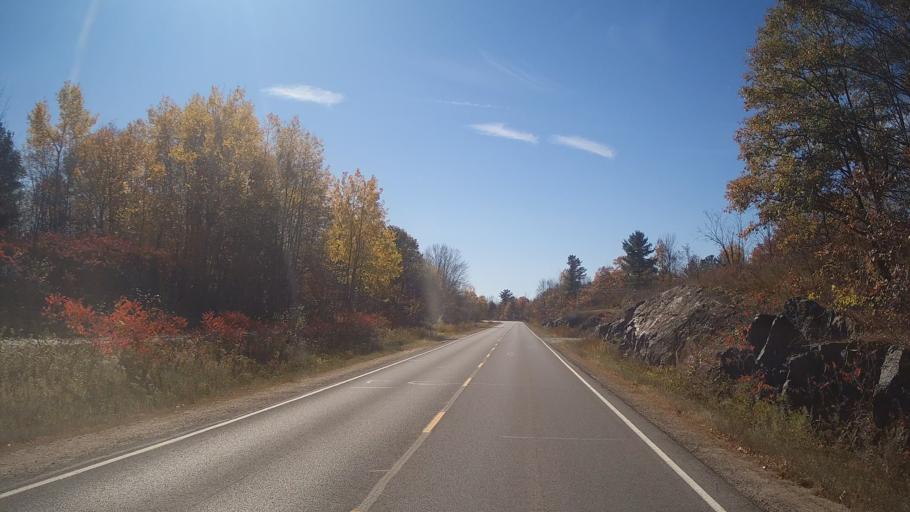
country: CA
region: Ontario
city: Kingston
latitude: 44.6712
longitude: -76.6737
